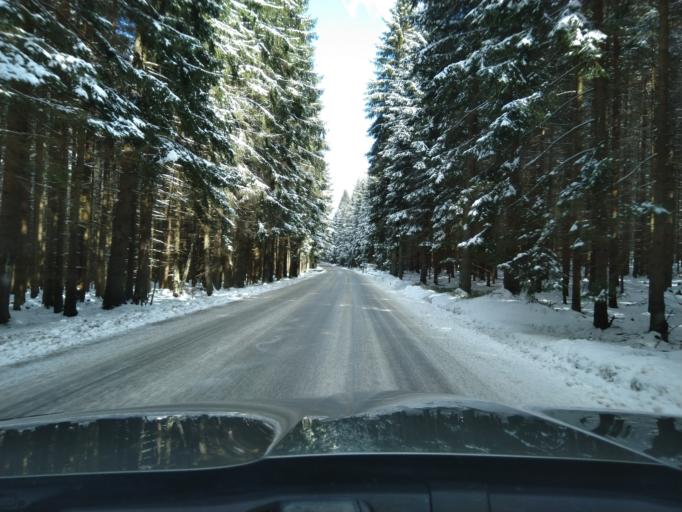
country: CZ
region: Jihocesky
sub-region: Okres Prachatice
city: Zdikov
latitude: 49.0531
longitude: 13.6943
